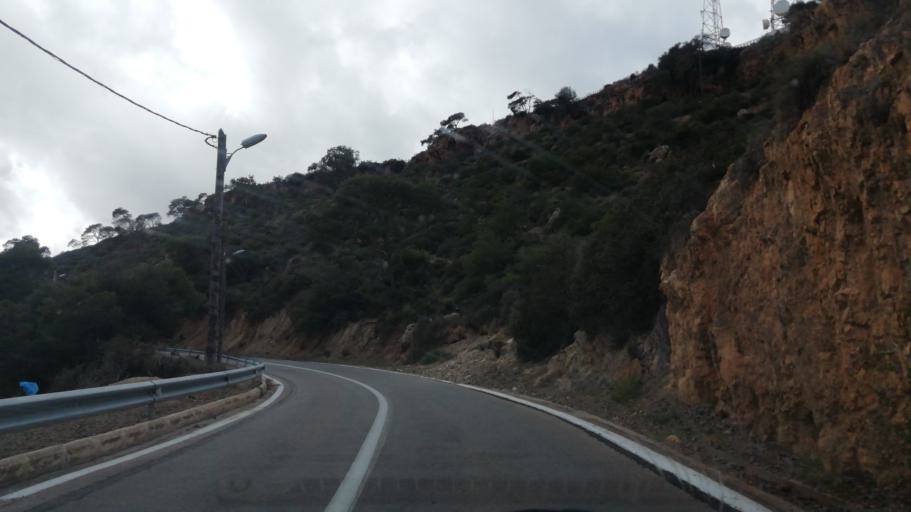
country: DZ
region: Oran
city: Oran
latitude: 35.7053
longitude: -0.6708
